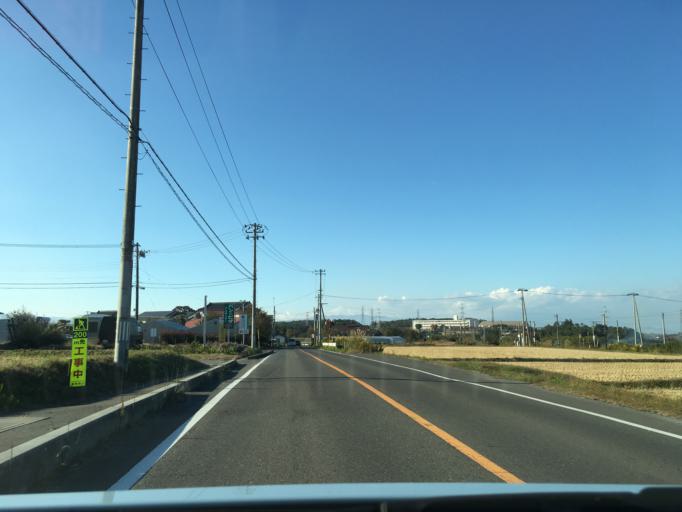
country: JP
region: Fukushima
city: Sukagawa
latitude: 37.3243
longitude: 140.3753
